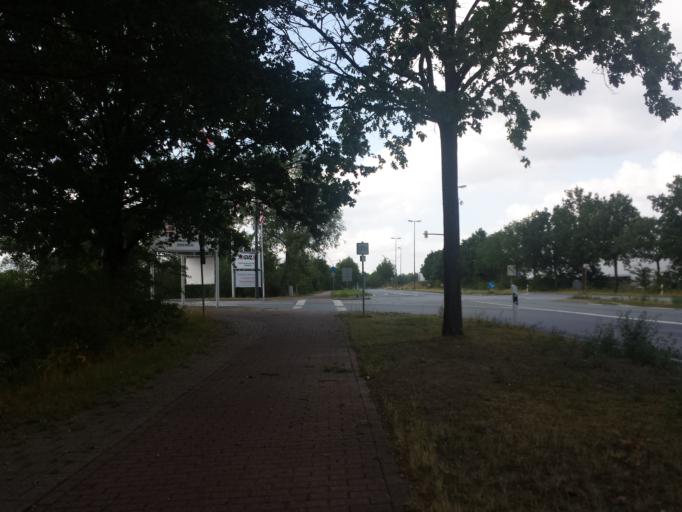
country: DE
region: Lower Saxony
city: Stuhr
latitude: 53.0814
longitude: 8.7350
